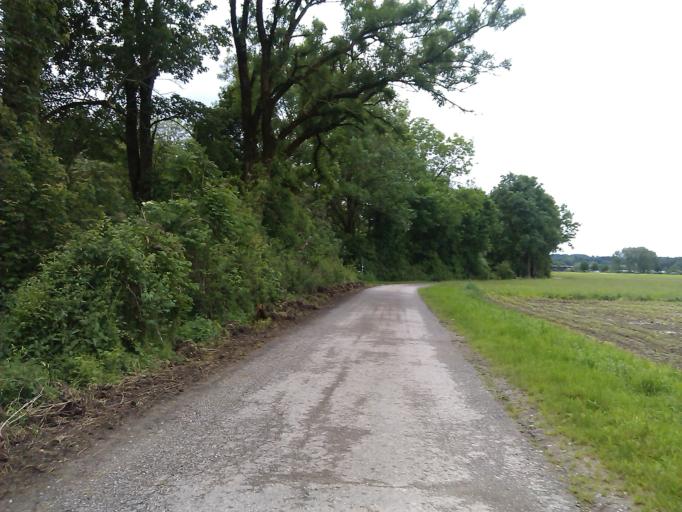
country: DE
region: Bavaria
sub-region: Swabia
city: Pforzen
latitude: 47.9405
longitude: 10.6141
